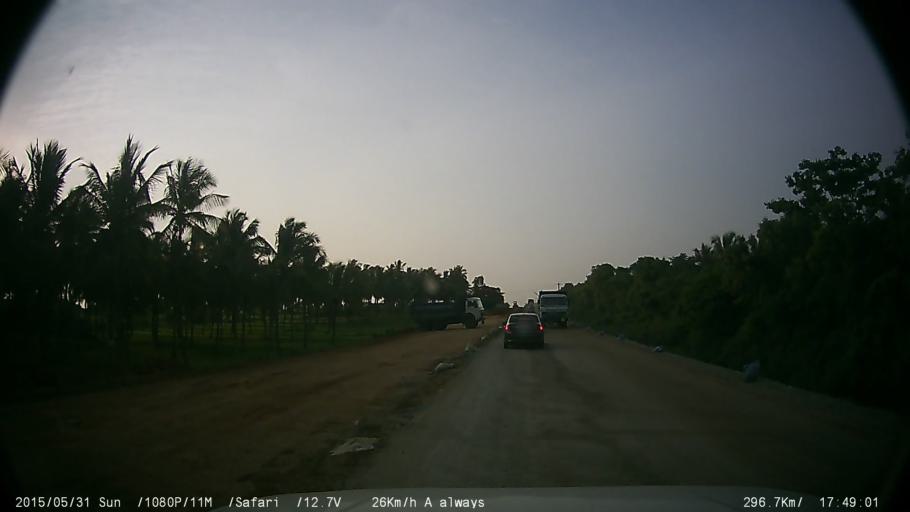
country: IN
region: Karnataka
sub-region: Mysore
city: Nanjangud
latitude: 11.9692
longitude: 76.6701
